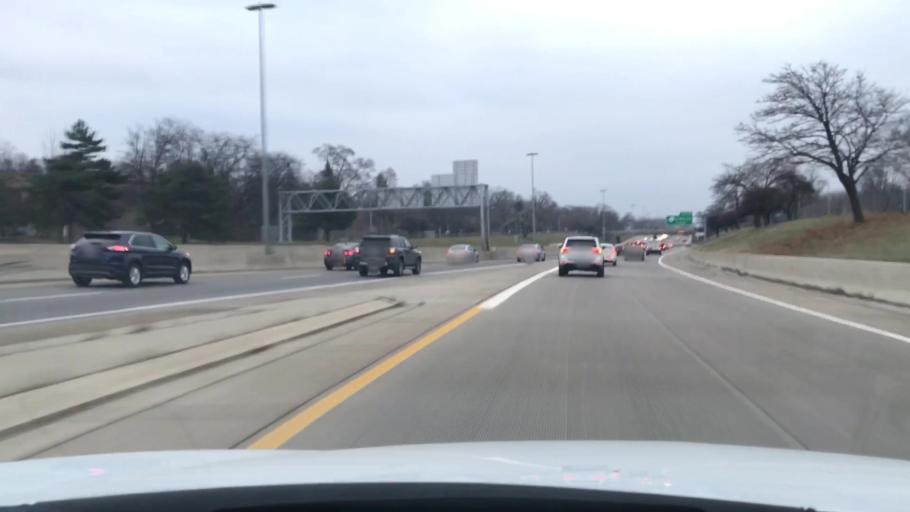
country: US
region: Michigan
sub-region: Oakland County
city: Southfield
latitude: 42.4548
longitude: -83.2203
